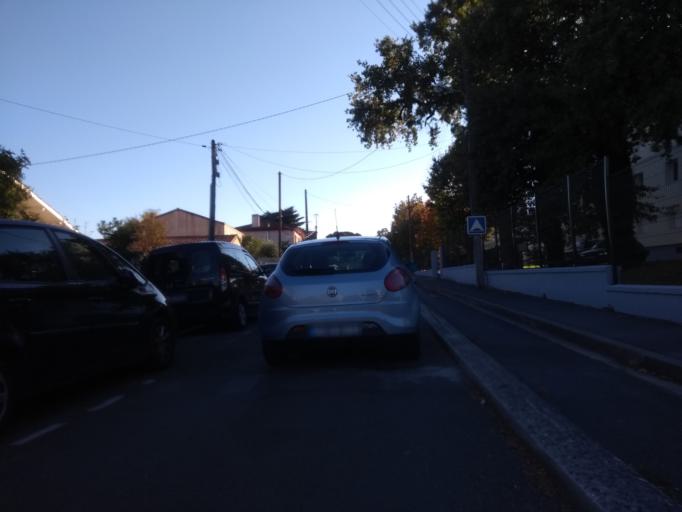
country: FR
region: Aquitaine
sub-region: Departement de la Gironde
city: Talence
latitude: 44.8046
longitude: -0.5885
